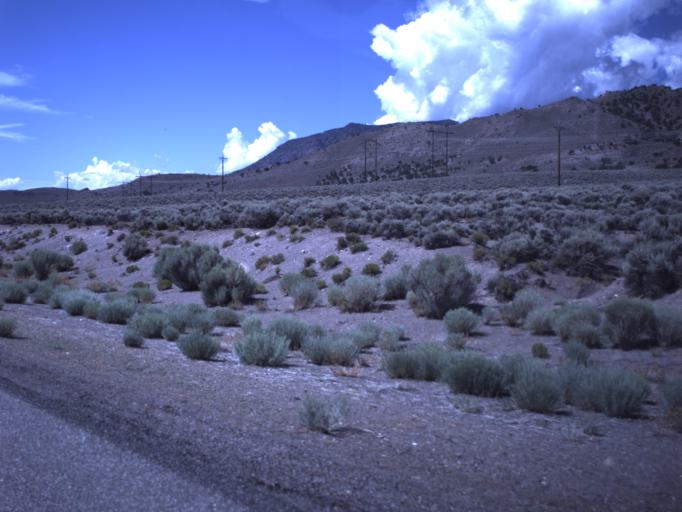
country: US
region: Utah
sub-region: Piute County
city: Junction
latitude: 38.3138
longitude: -112.2216
